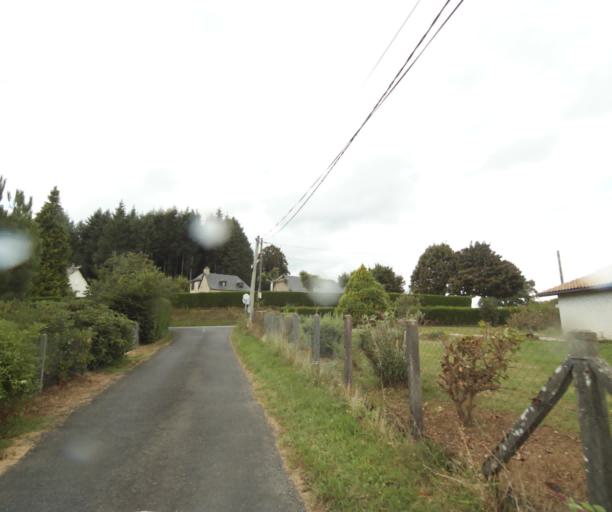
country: FR
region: Limousin
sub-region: Departement de la Correze
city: Sainte-Fortunade
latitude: 45.1832
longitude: 1.8130
